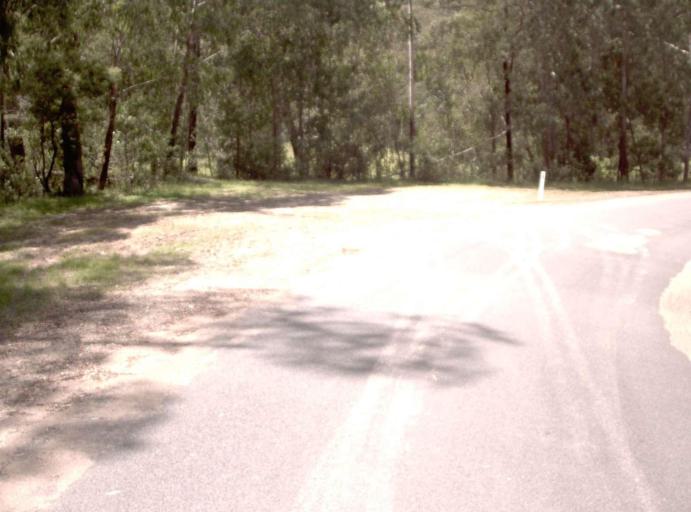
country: AU
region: New South Wales
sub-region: Bombala
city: Bombala
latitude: -37.4337
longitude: 148.9895
